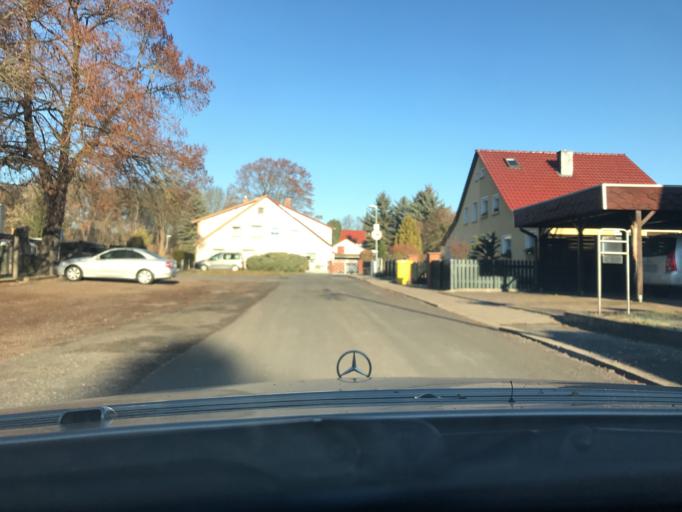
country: DE
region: Thuringia
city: Muehlhausen
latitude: 51.2325
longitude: 10.4490
